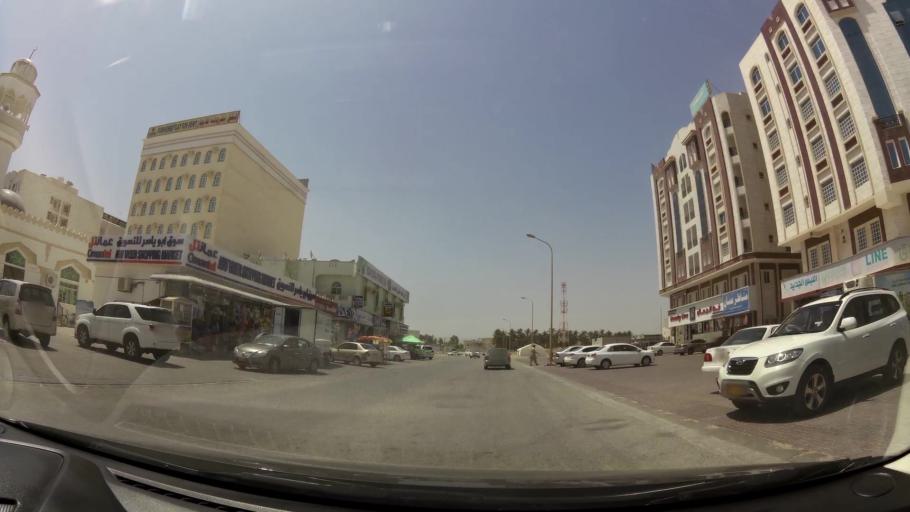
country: OM
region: Zufar
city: Salalah
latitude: 17.0508
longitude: 54.1534
